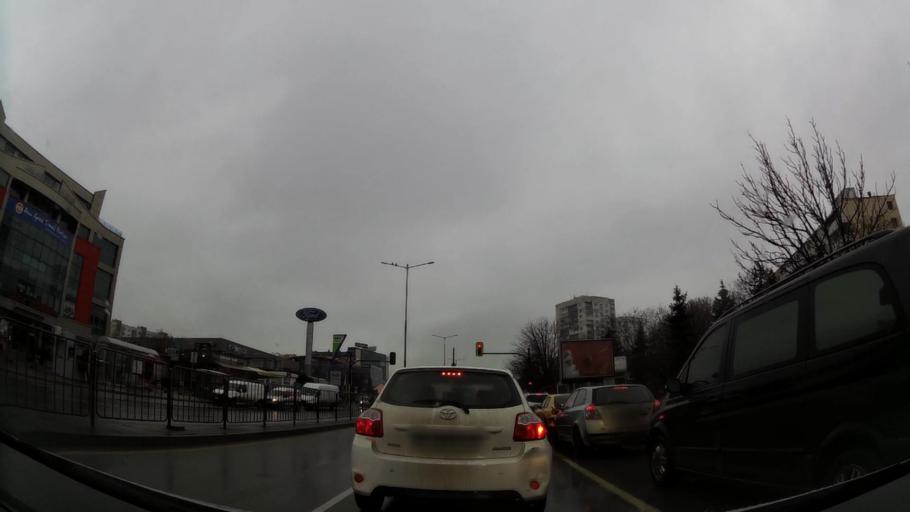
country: BG
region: Sofia-Capital
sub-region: Stolichna Obshtina
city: Sofia
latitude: 42.6525
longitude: 23.3798
